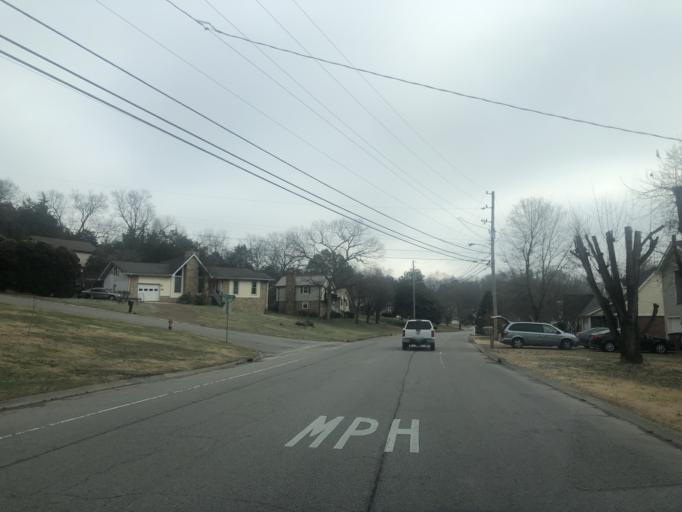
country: US
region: Tennessee
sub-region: Rutherford County
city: La Vergne
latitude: 36.0738
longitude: -86.6623
